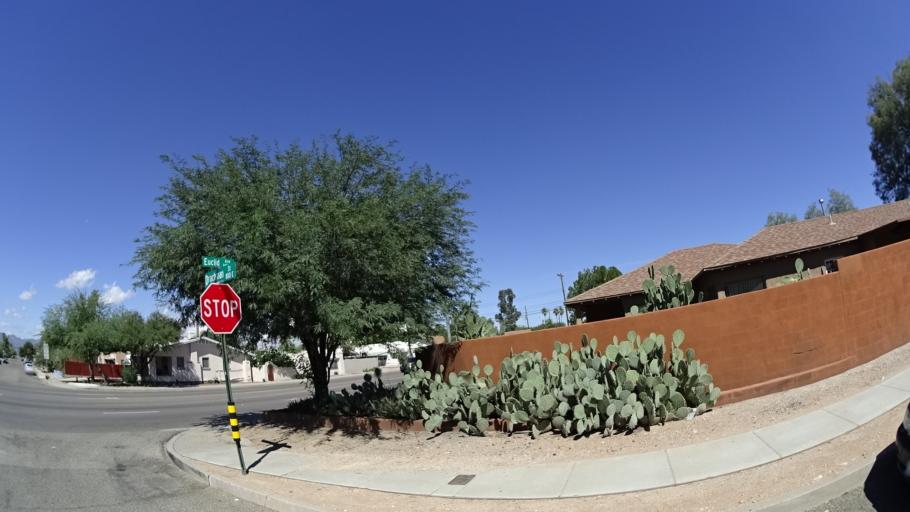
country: US
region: Arizona
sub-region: Pima County
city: Tucson
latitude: 32.2396
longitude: -110.9592
